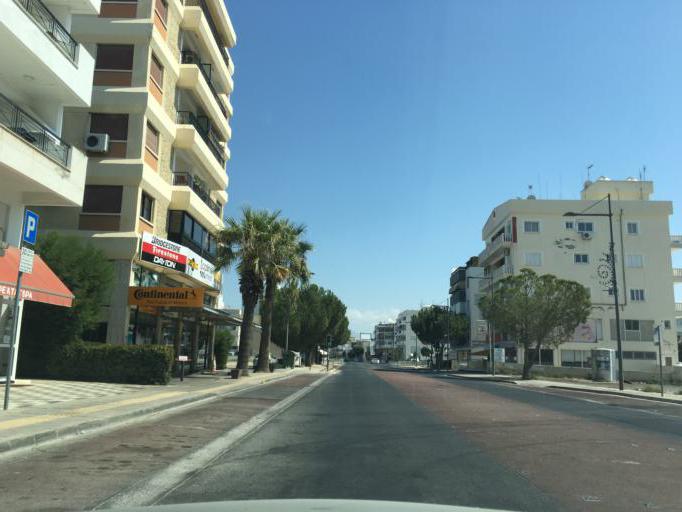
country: CY
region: Lefkosia
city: Nicosia
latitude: 35.1574
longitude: 33.3151
